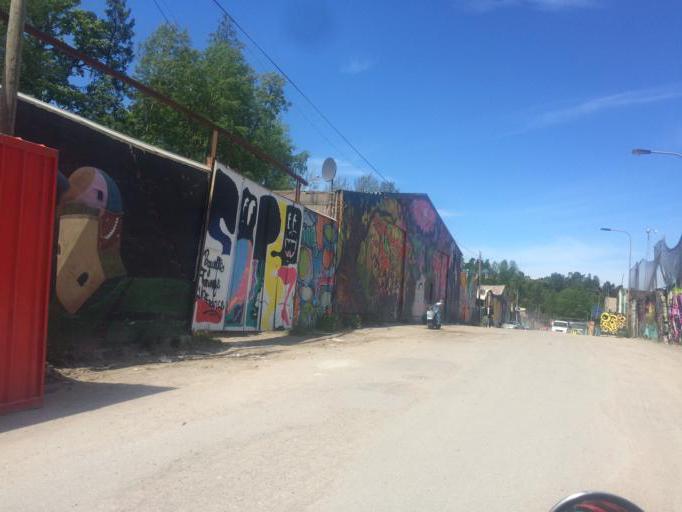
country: SE
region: Stockholm
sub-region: Stockholms Kommun
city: Arsta
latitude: 59.2491
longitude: 18.0421
